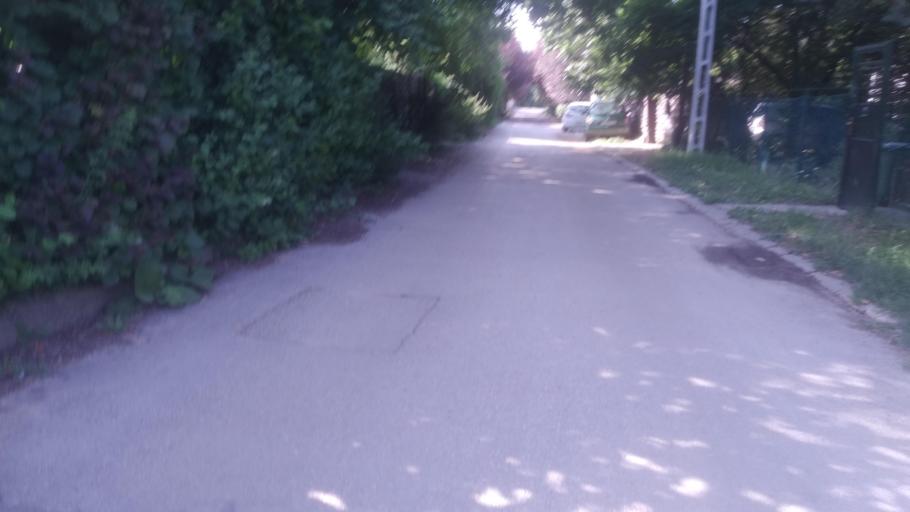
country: HU
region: Pest
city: Solymar
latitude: 47.5675
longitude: 18.9453
